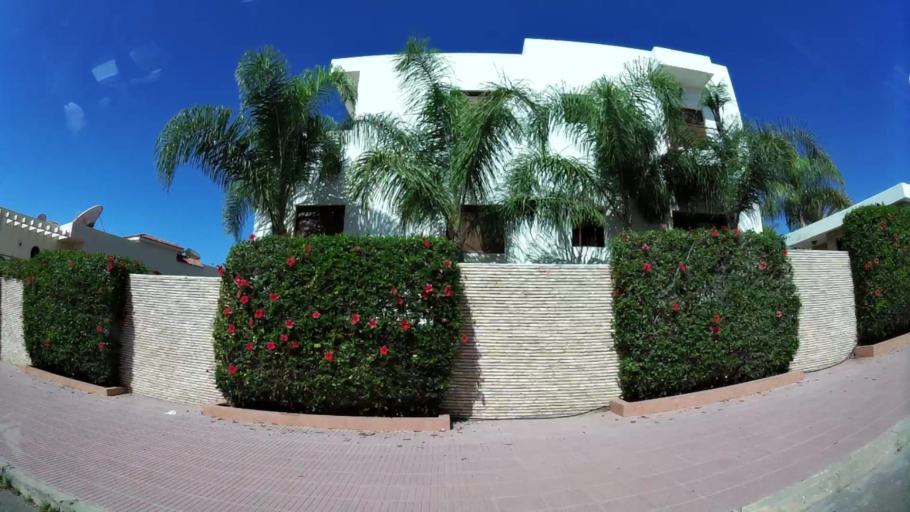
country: MA
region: Souss-Massa-Draa
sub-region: Agadir-Ida-ou-Tnan
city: Agadir
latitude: 30.4428
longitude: -9.5812
